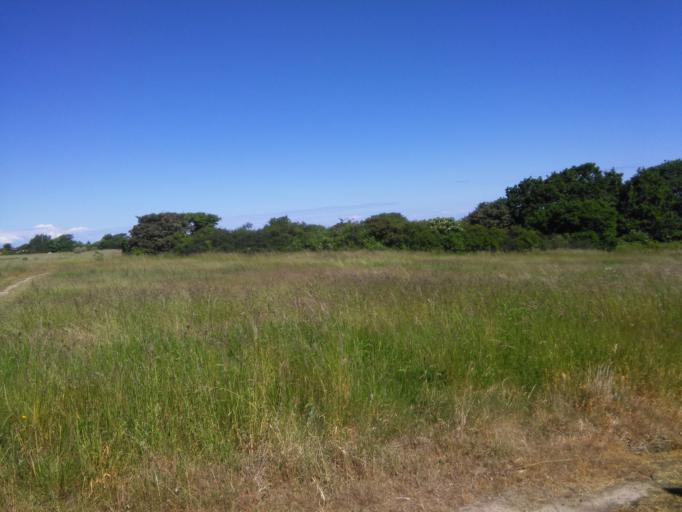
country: DK
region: Capital Region
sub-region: Bornholm Kommune
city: Ronne
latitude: 55.2813
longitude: 14.7894
